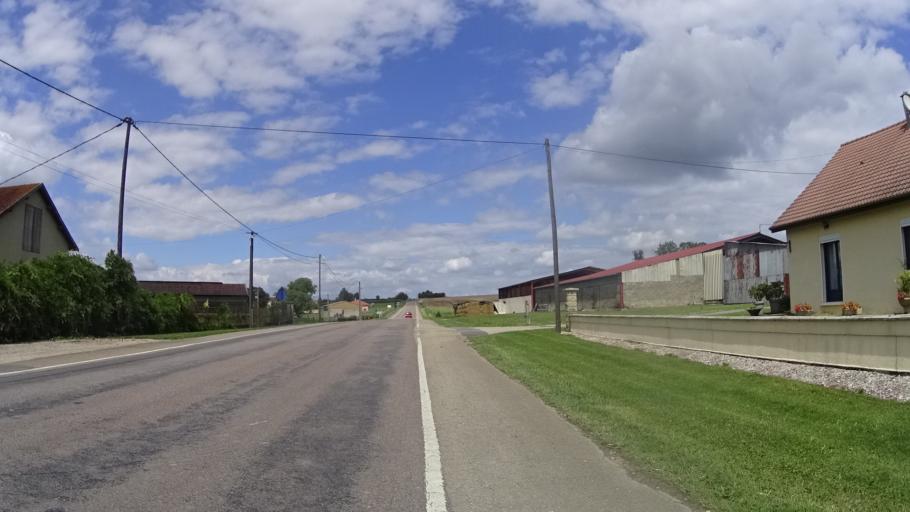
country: FR
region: Champagne-Ardenne
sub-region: Departement de la Haute-Marne
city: Montier-en-Der
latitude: 48.4869
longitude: 4.7597
